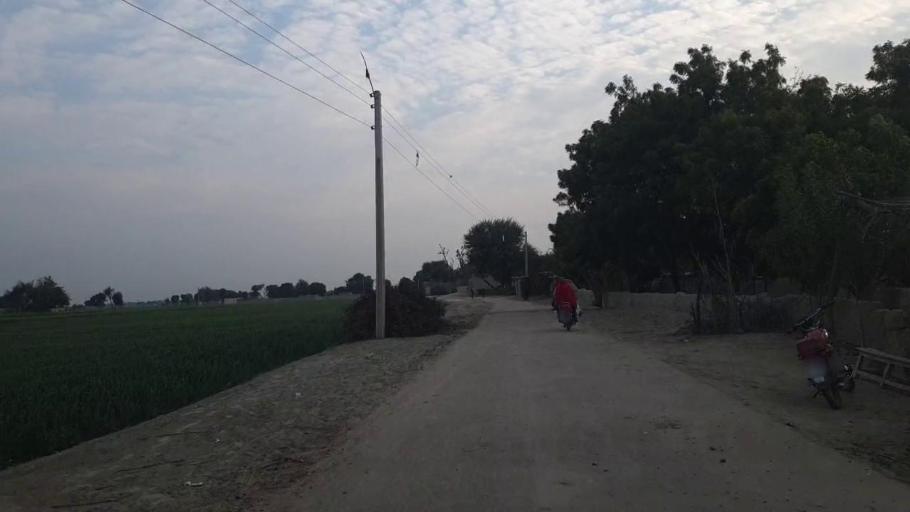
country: PK
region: Sindh
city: Shahpur Chakar
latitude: 26.0892
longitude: 68.5383
